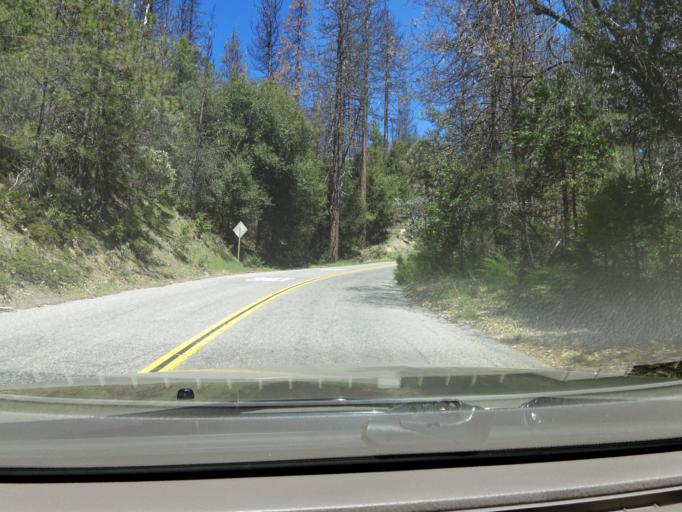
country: US
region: California
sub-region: Madera County
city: Oakhurst
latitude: 37.3216
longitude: -119.5566
